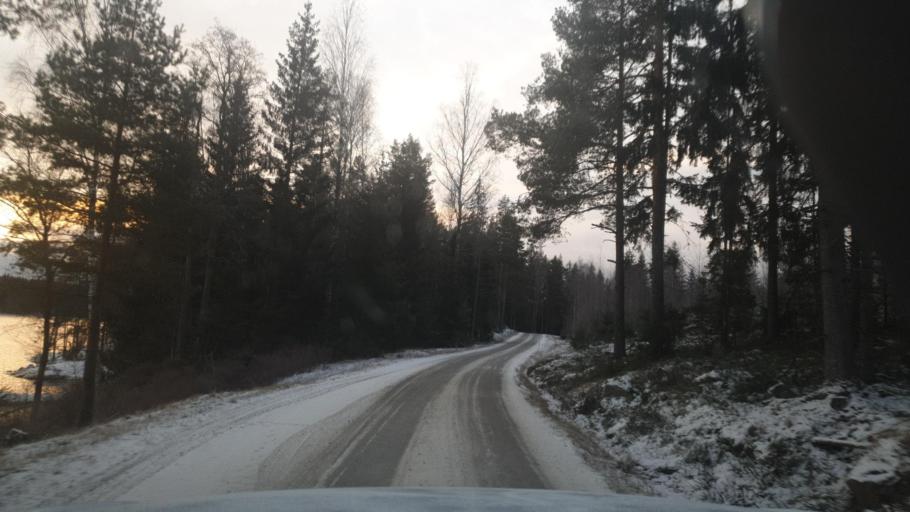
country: SE
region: Vaermland
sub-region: Grums Kommun
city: Grums
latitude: 59.5062
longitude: 12.9269
